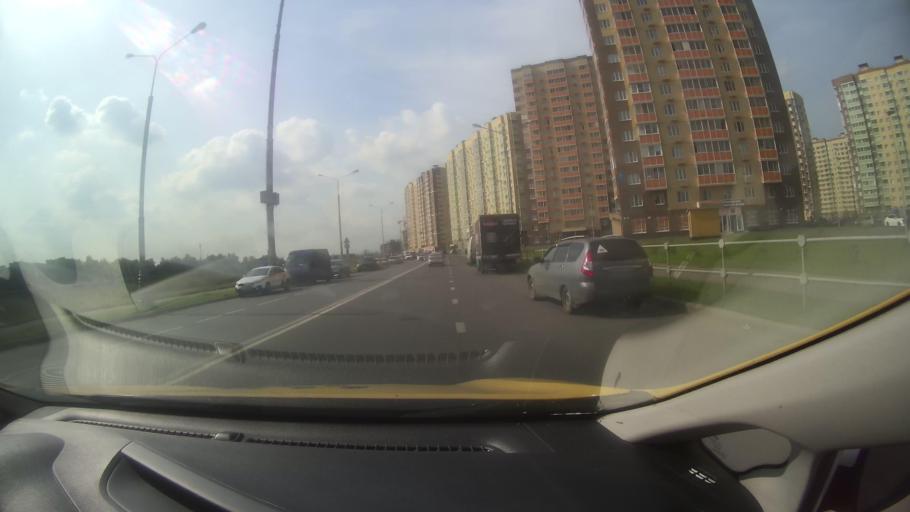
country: RU
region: Moskovskaya
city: Tomilino
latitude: 55.6965
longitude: 37.9637
